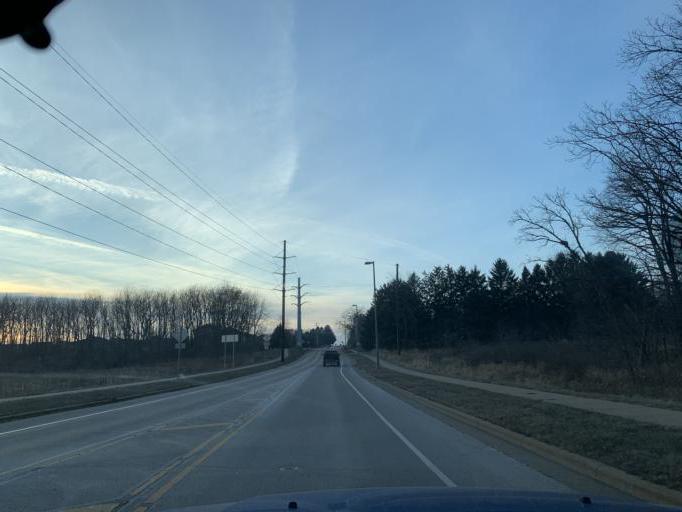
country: US
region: Wisconsin
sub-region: Dane County
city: Verona
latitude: 43.0458
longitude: -89.5355
